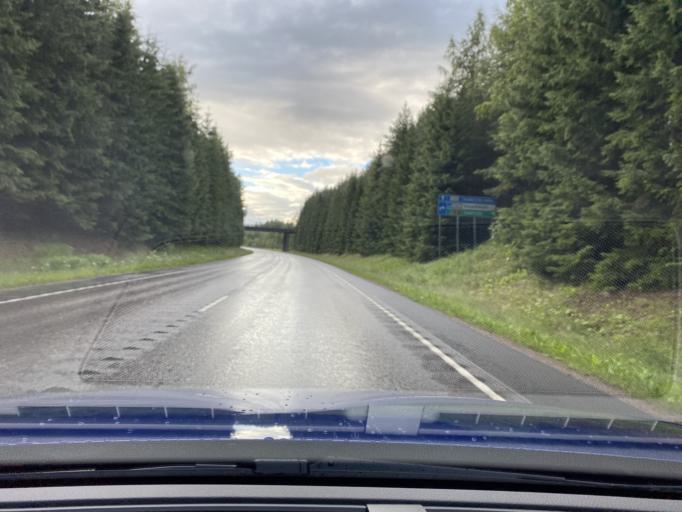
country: FI
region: Uusimaa
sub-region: Helsinki
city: Hyvinge
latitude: 60.6591
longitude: 24.7984
